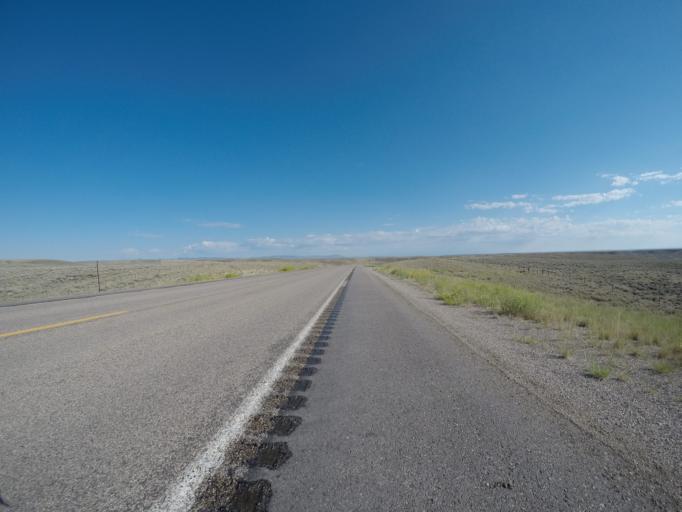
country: US
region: Wyoming
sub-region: Lincoln County
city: Kemmerer
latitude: 42.0393
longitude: -110.1576
